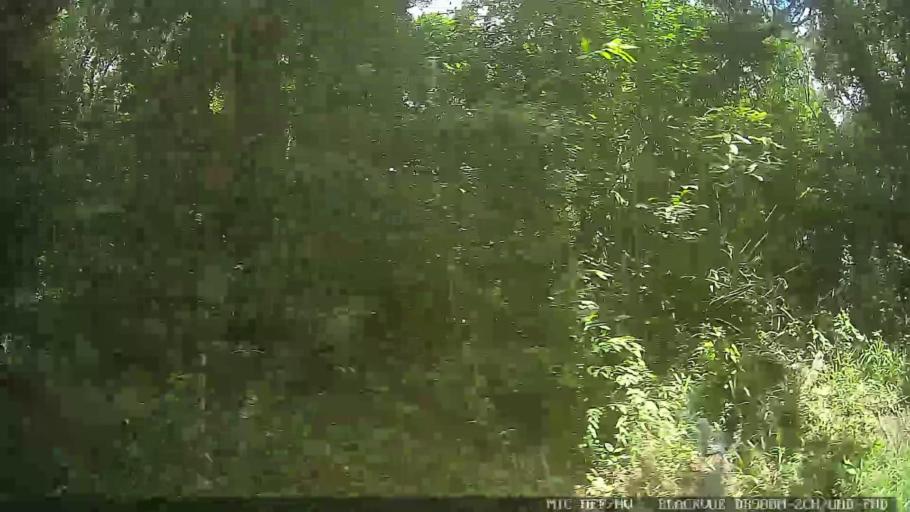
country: BR
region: Minas Gerais
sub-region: Extrema
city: Extrema
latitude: -22.8733
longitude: -46.3234
